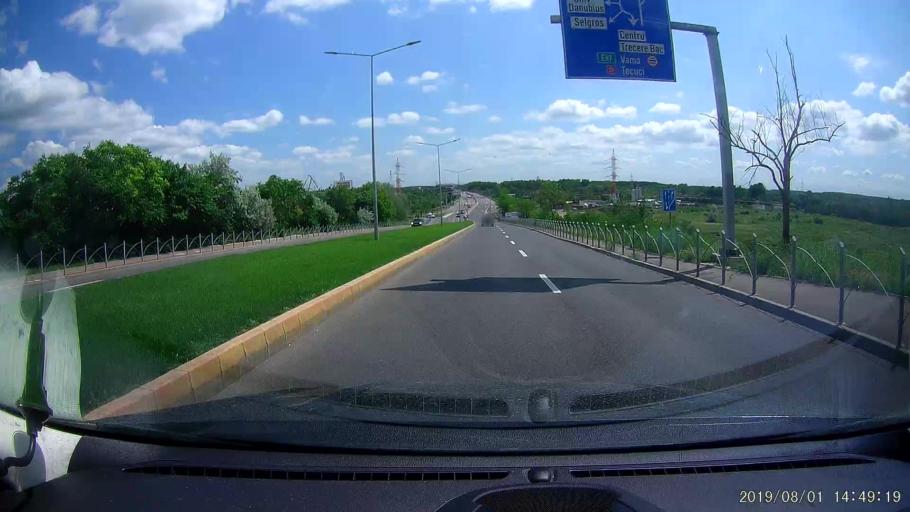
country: RO
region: Galati
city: Galati
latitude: 45.4064
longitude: 28.0151
